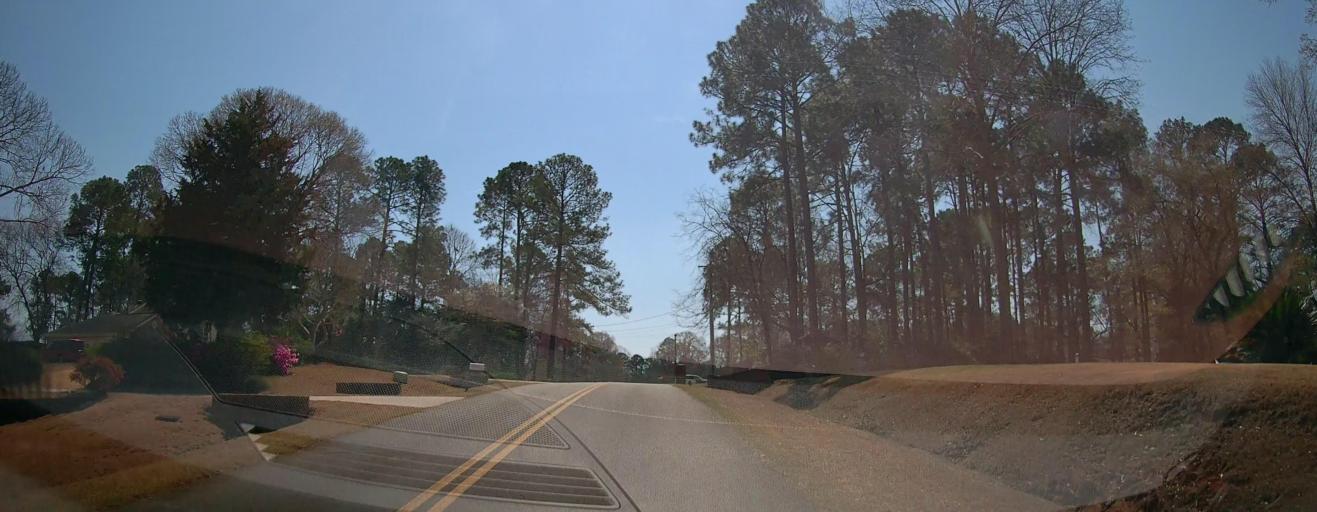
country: US
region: Georgia
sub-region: Houston County
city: Centerville
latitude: 32.5945
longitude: -83.6960
